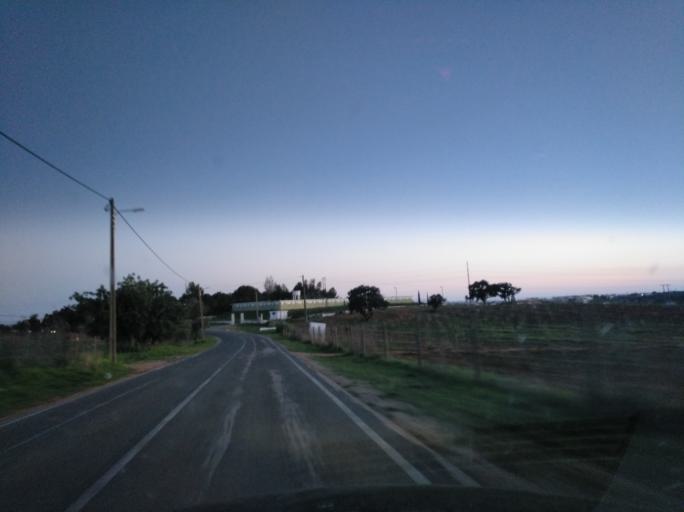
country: PT
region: Faro
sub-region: Vila Real de Santo Antonio
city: Monte Gordo
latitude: 37.1919
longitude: -7.5135
